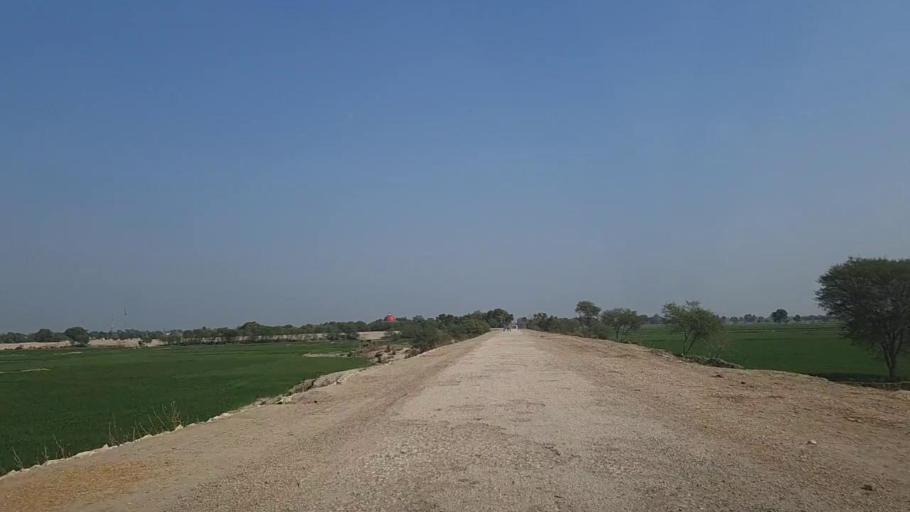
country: PK
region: Sindh
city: Naushahro Firoz
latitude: 26.8601
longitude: 67.9699
